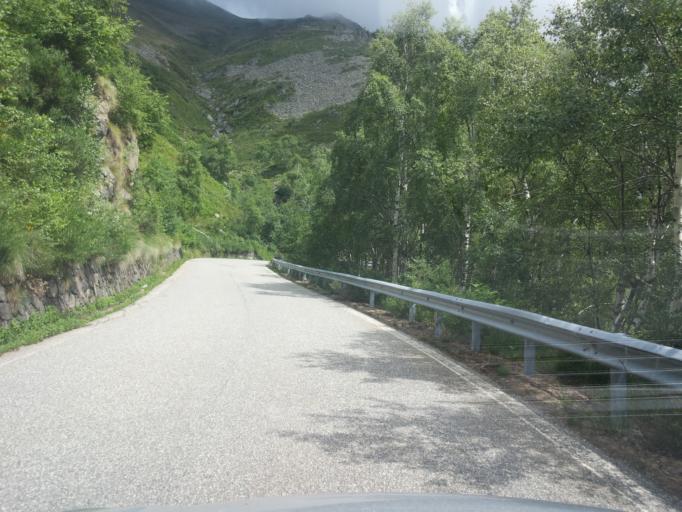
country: IT
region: Piedmont
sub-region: Provincia di Biella
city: Sagliano Micca
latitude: 45.6567
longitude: 8.0519
